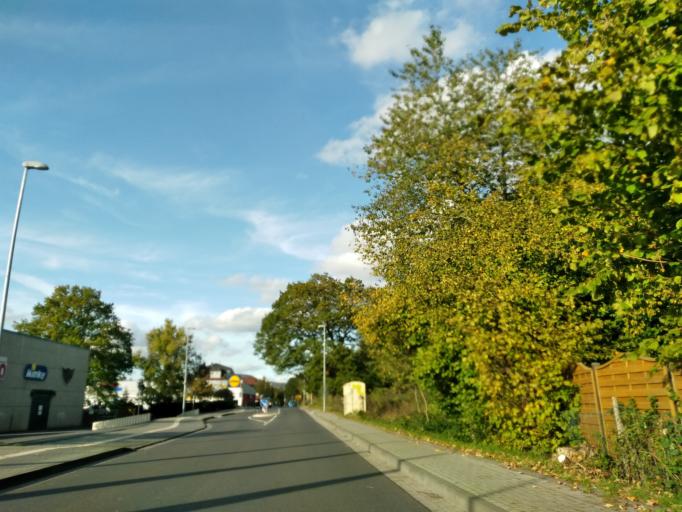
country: DE
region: Rheinland-Pfalz
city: Rheinbreitbach
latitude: 50.6259
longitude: 7.2300
